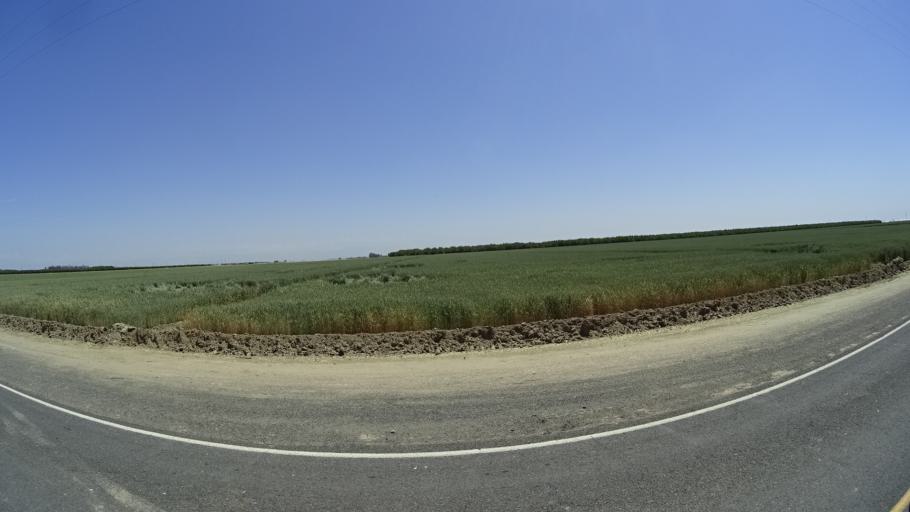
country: US
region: California
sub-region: Kings County
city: Armona
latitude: 36.2323
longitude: -119.7088
